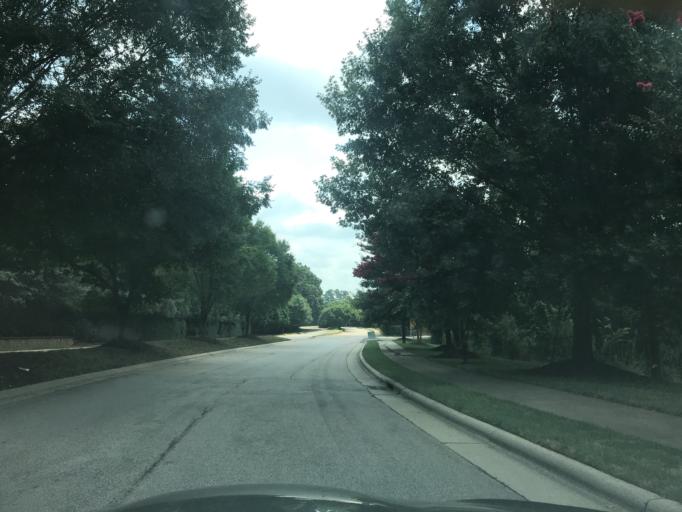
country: US
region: North Carolina
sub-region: Wake County
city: Wake Forest
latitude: 35.9259
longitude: -78.5860
